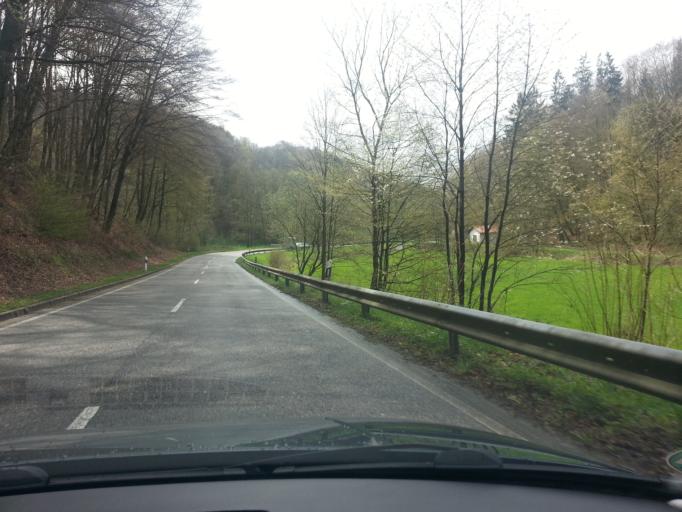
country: DE
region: Rheinland-Pfalz
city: Biedershausen
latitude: 49.3074
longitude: 7.4940
